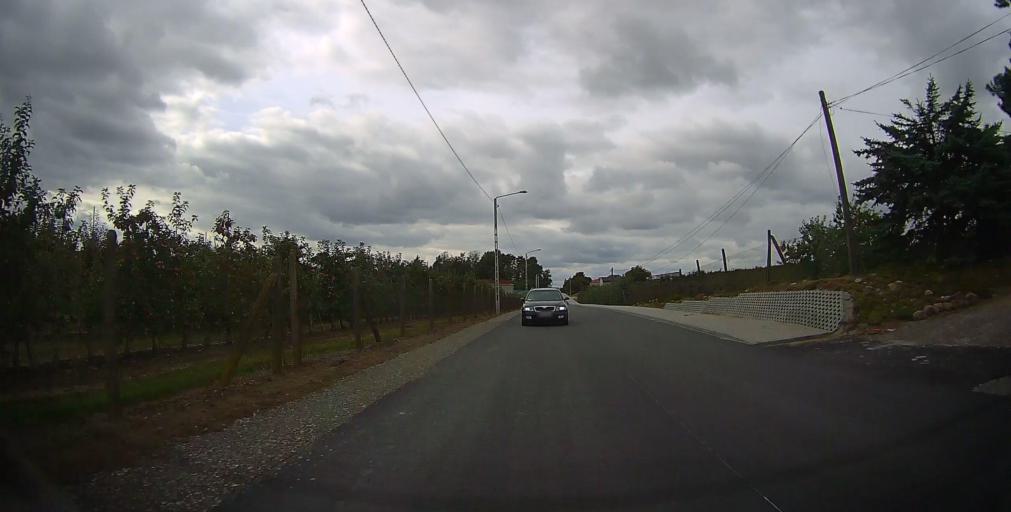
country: PL
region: Masovian Voivodeship
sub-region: Powiat grojecki
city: Belsk Duzy
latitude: 51.8125
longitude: 20.8342
